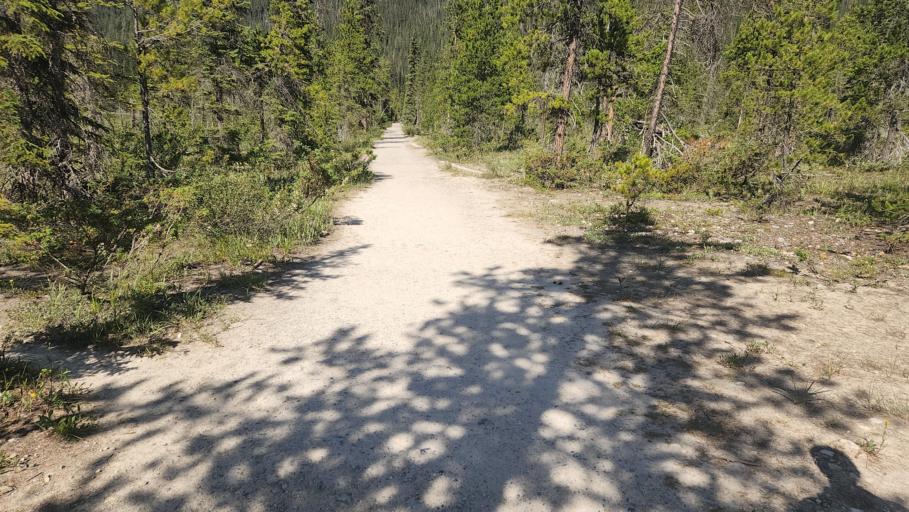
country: CA
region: Alberta
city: Lake Louise
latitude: 51.4510
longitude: -116.5273
